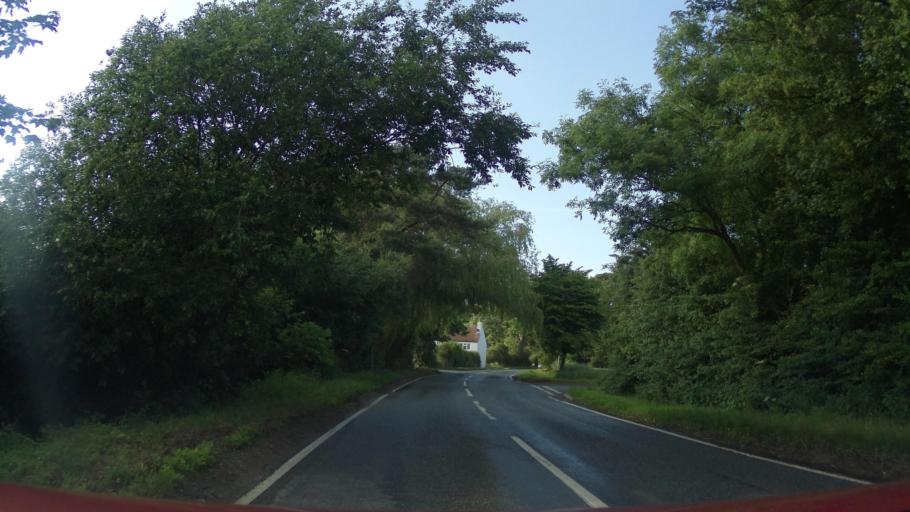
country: GB
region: England
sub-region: Lincolnshire
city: Great Gonerby
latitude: 53.0463
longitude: -0.6459
